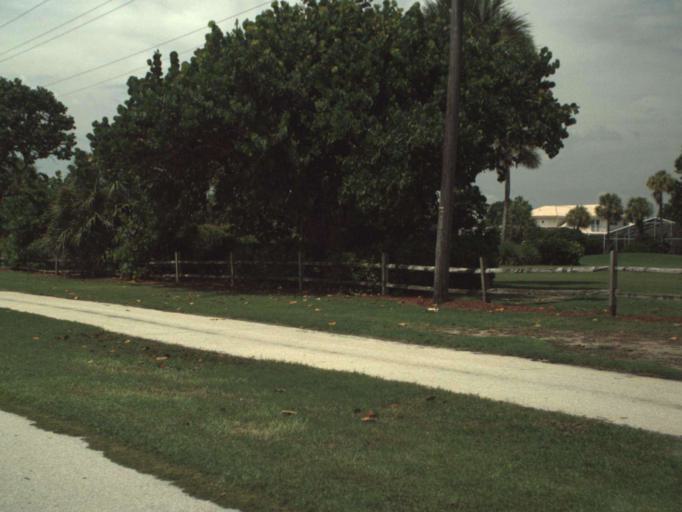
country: US
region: Florida
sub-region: Palm Beach County
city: Boca Raton
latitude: 26.3601
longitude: -80.0703
